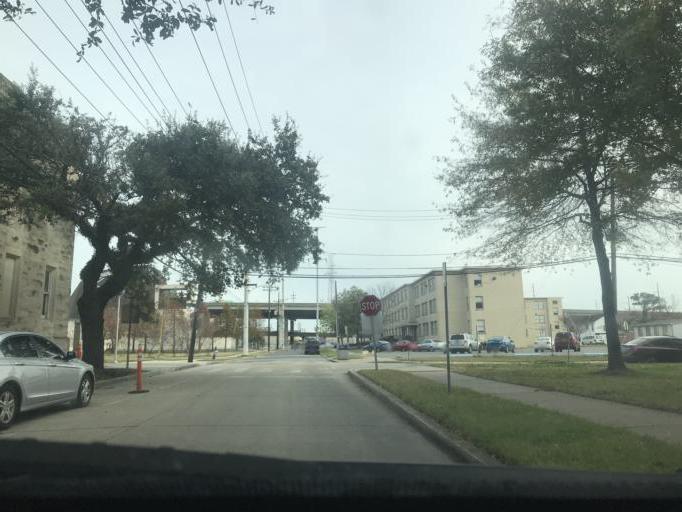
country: US
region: Louisiana
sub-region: Orleans Parish
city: New Orleans
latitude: 29.9641
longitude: -90.1065
